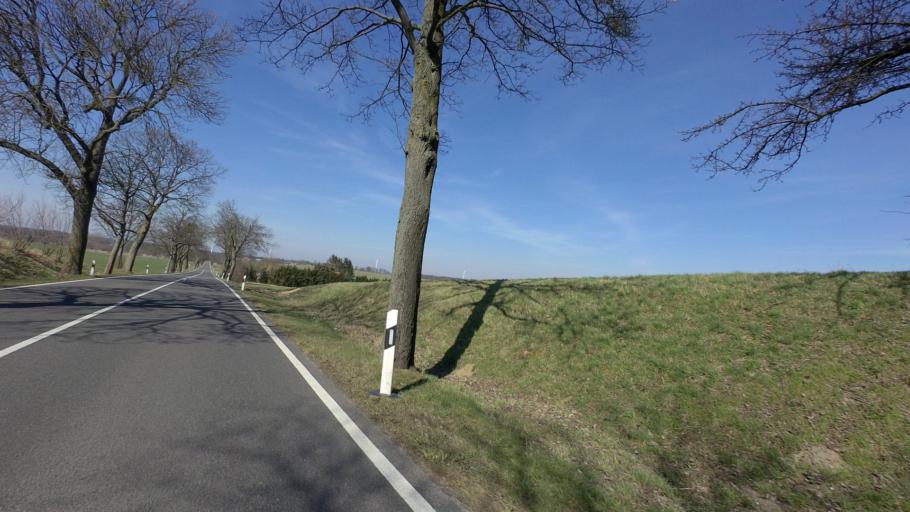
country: DE
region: Brandenburg
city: Protzel
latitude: 52.6162
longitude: 14.0195
